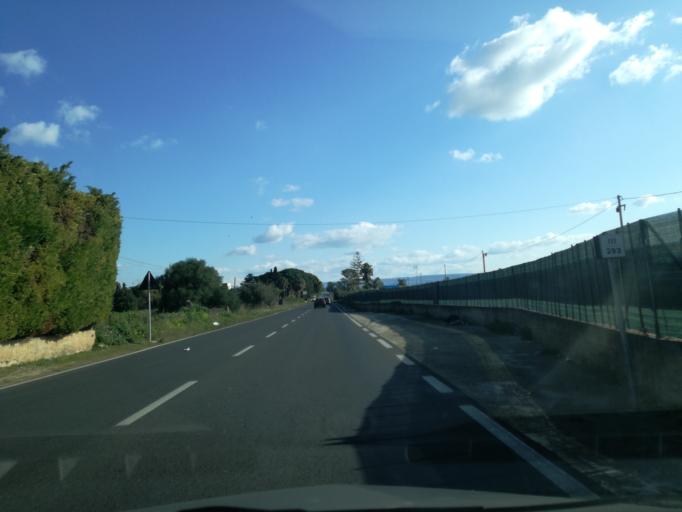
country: IT
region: Sicily
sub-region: Ragusa
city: Vittoria
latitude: 36.9616
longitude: 14.4957
